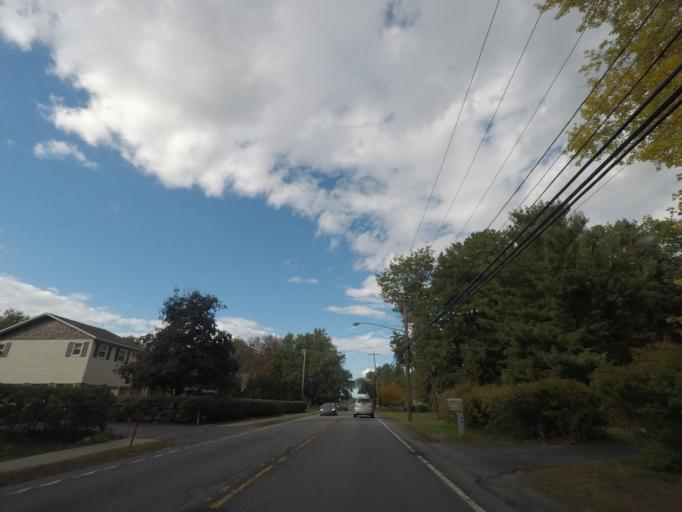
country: US
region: New York
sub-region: Albany County
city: Voorheesville
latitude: 42.7197
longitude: -73.9335
